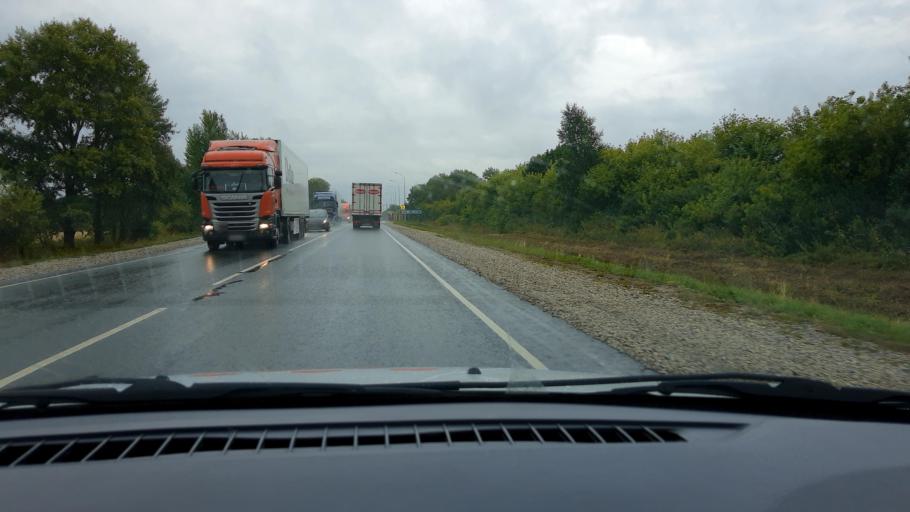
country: RU
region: Chuvashia
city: Tsivil'sk
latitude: 55.7900
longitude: 47.6862
